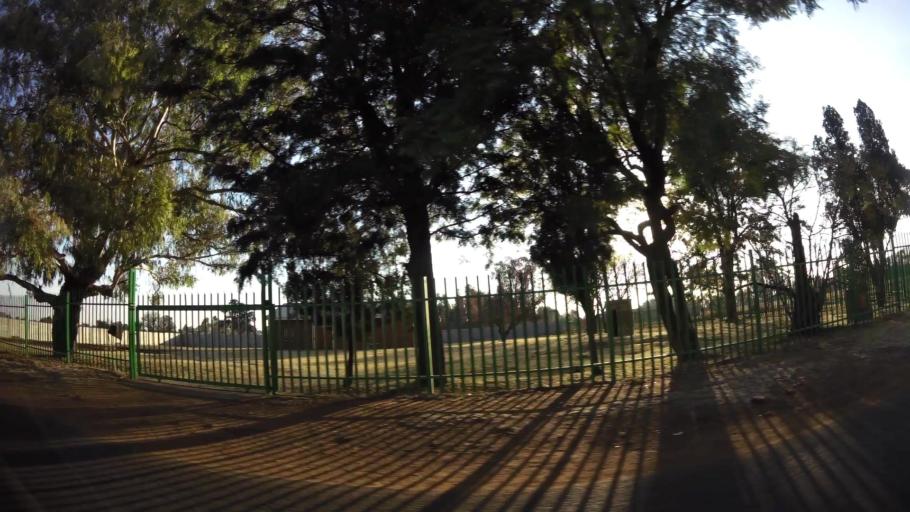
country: ZA
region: Gauteng
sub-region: West Rand District Municipality
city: Randfontein
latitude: -26.2046
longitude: 27.6483
